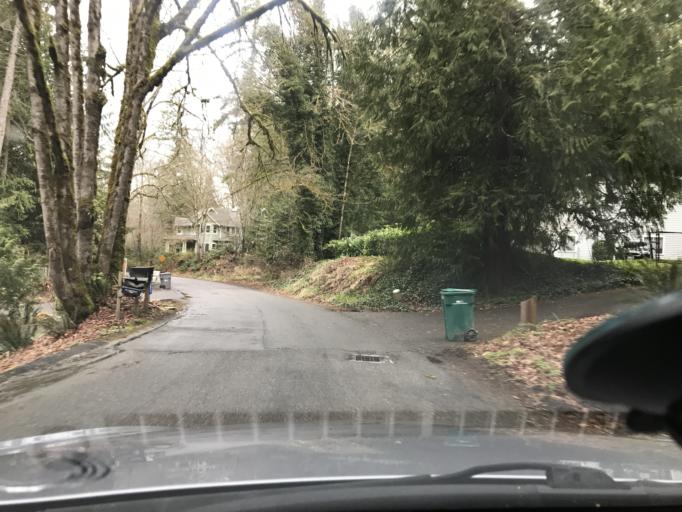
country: US
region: Washington
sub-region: King County
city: Ames Lake
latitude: 47.6453
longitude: -121.9545
